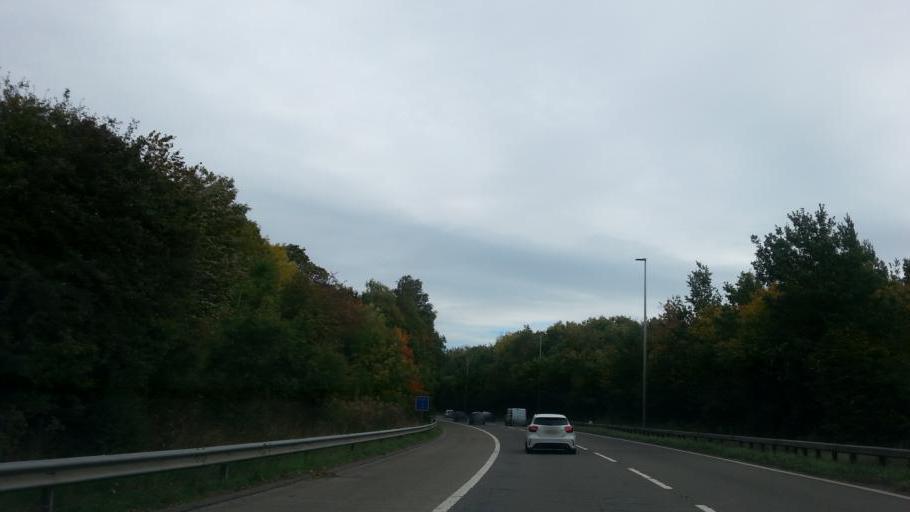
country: GB
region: England
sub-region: City and Borough of Leeds
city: Gildersome
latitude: 53.7463
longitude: -1.6289
